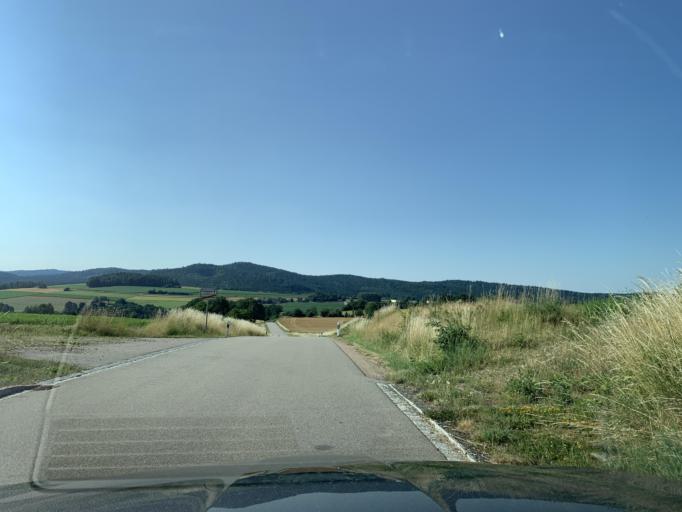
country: DE
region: Bavaria
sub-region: Upper Palatinate
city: Dieterskirchen
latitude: 49.4123
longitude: 12.4128
